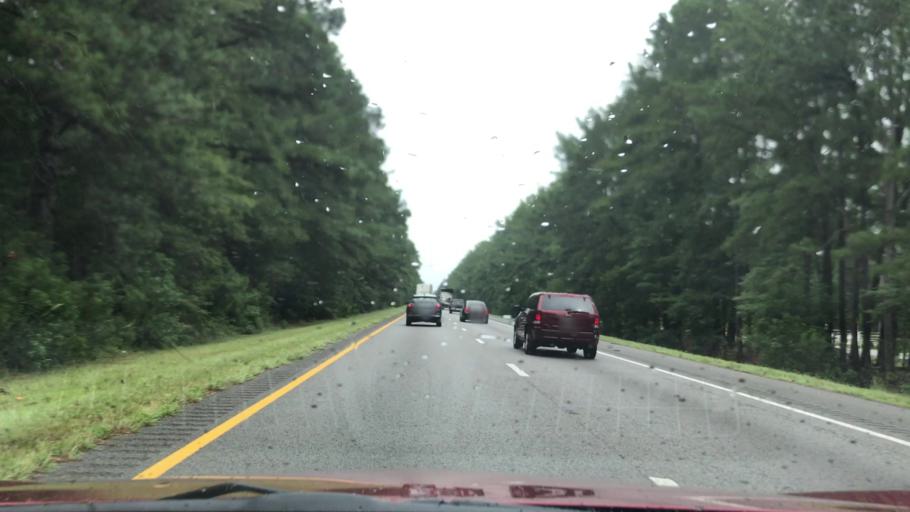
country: US
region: South Carolina
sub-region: Dorchester County
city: Ridgeville
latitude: 33.1082
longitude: -80.2557
